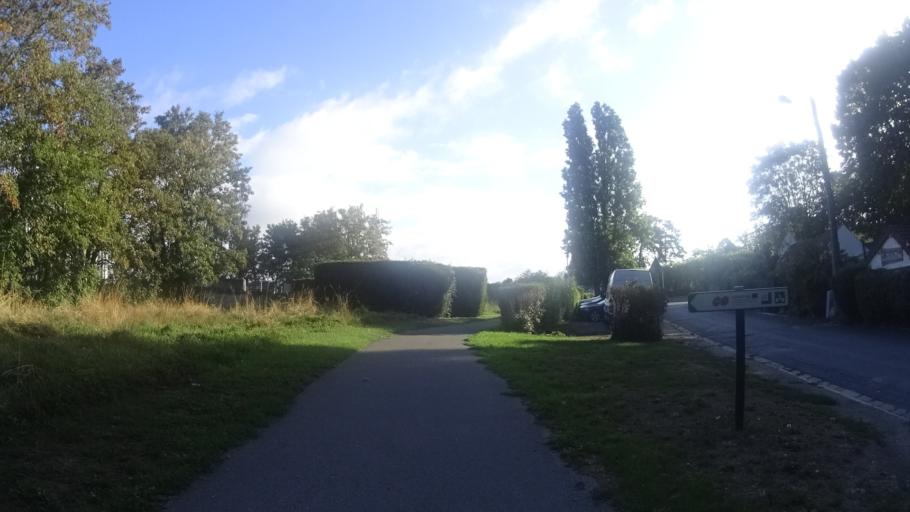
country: FR
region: Picardie
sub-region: Departement de l'Oise
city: Verberie
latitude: 49.3111
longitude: 2.7248
